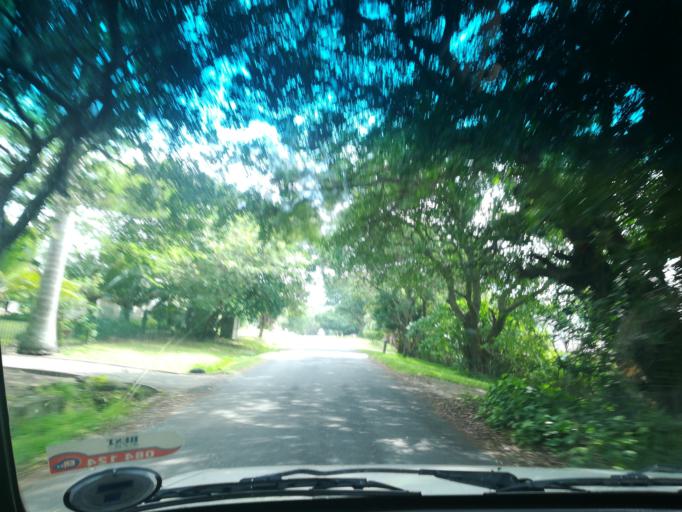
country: ZA
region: KwaZulu-Natal
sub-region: Ugu District Municipality
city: Scottburgh
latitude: -30.3883
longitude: 30.6912
